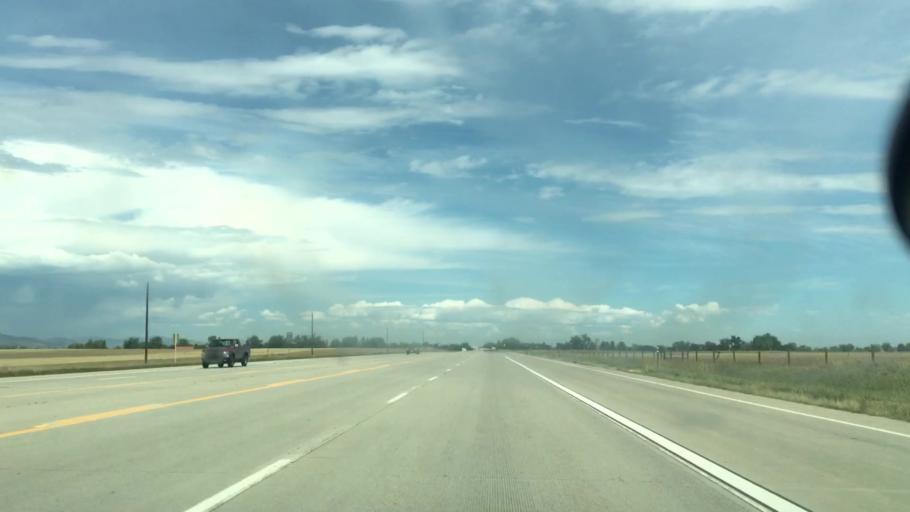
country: US
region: Colorado
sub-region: Boulder County
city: Longmont
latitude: 40.2188
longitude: -105.1023
